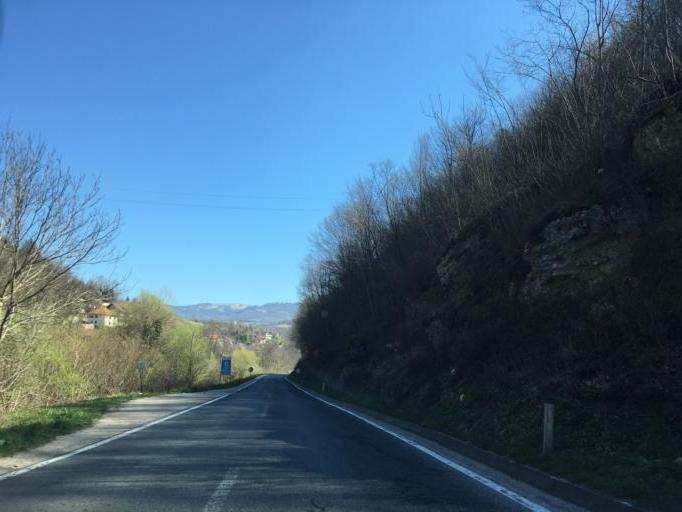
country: BA
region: Federation of Bosnia and Herzegovina
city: Jajce
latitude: 44.3450
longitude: 17.2866
